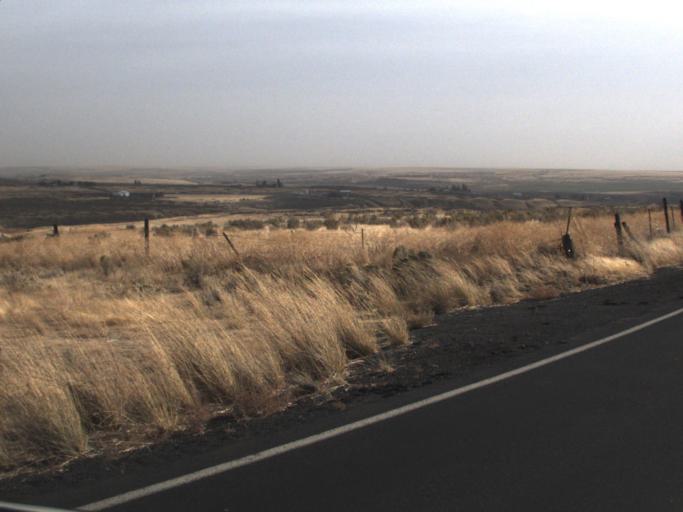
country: US
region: Washington
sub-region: Adams County
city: Ritzville
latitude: 47.3562
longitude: -118.6994
